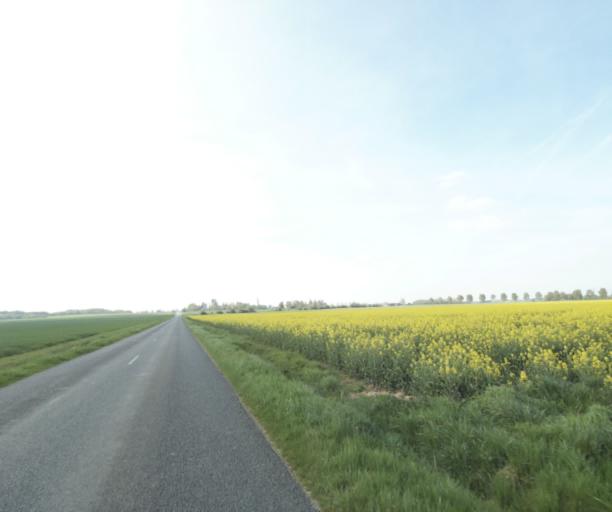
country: FR
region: Ile-de-France
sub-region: Departement de Seine-et-Marne
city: Nangis
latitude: 48.5750
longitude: 3.0120
